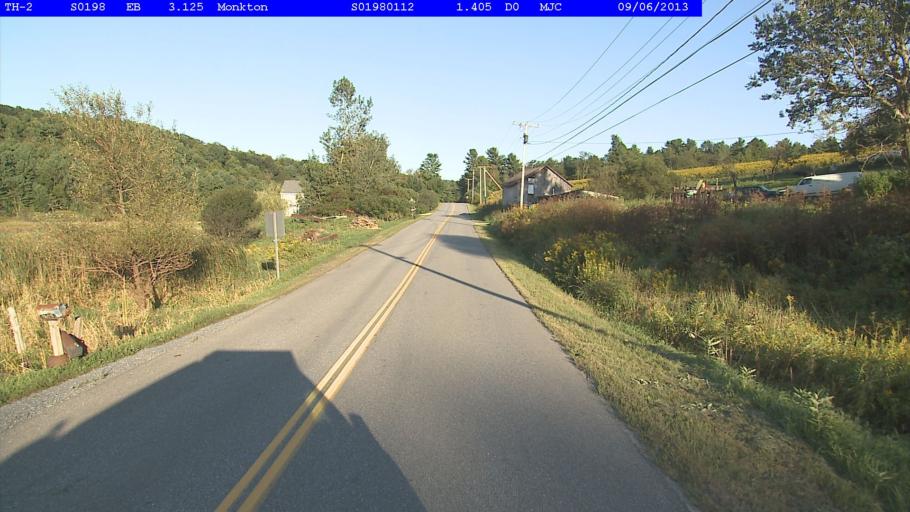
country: US
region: Vermont
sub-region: Chittenden County
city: Hinesburg
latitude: 44.2467
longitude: -73.1722
